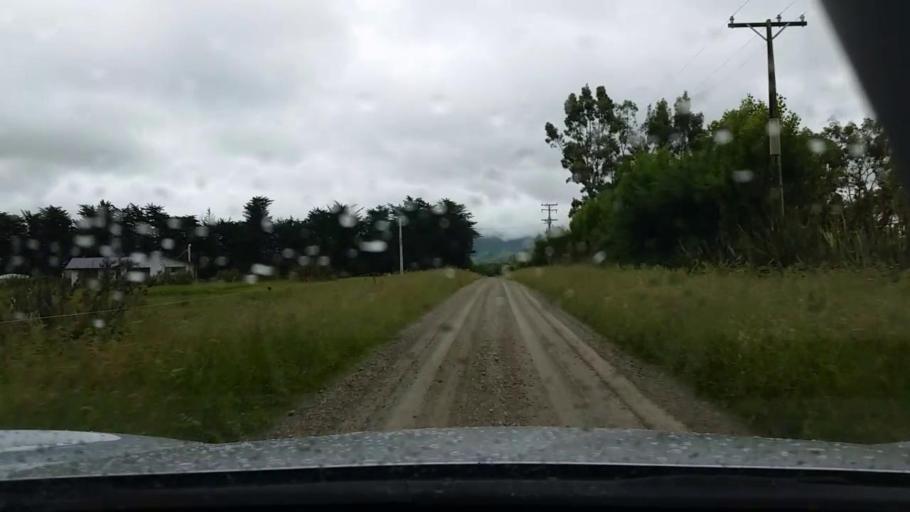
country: NZ
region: Southland
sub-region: Gore District
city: Gore
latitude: -46.0717
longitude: 168.9584
